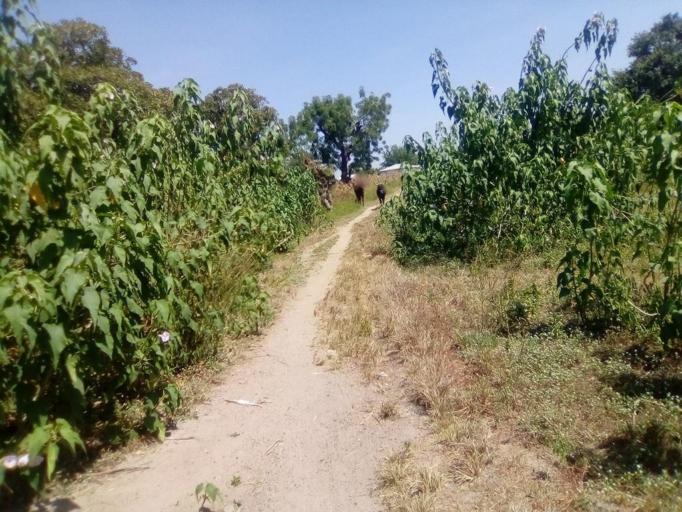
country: GH
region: Upper East
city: Bawku
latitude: 11.0945
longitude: -0.0714
